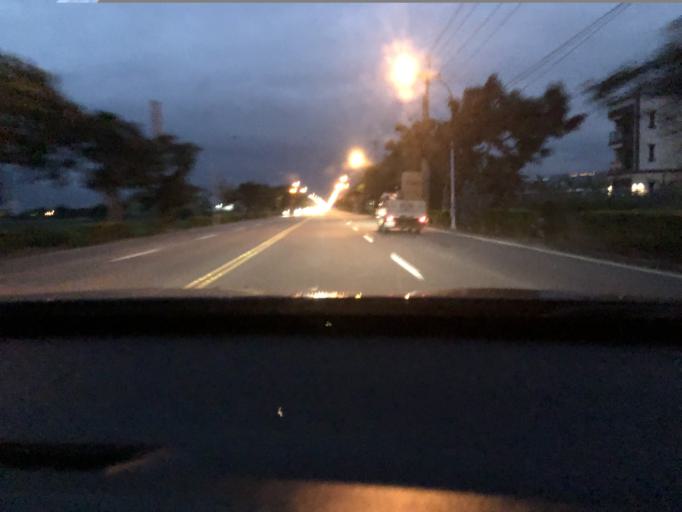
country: TW
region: Taiwan
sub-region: Hualien
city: Hualian
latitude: 23.9478
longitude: 121.5674
